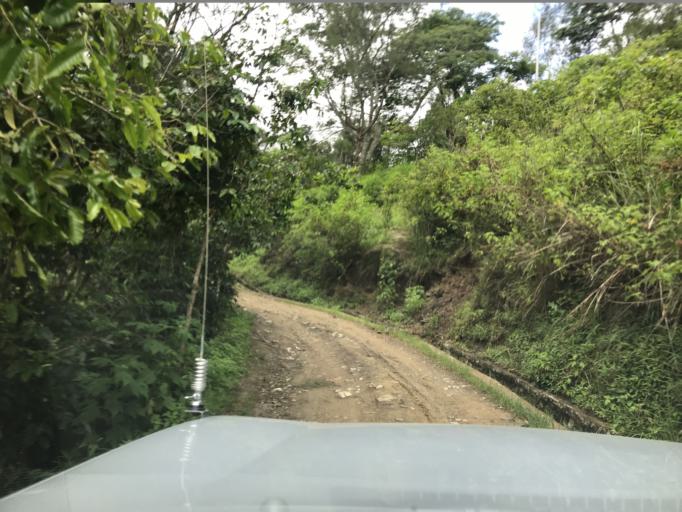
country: TL
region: Aileu
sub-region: Aileu Villa
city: Aileu
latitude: -8.8581
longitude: 125.5758
